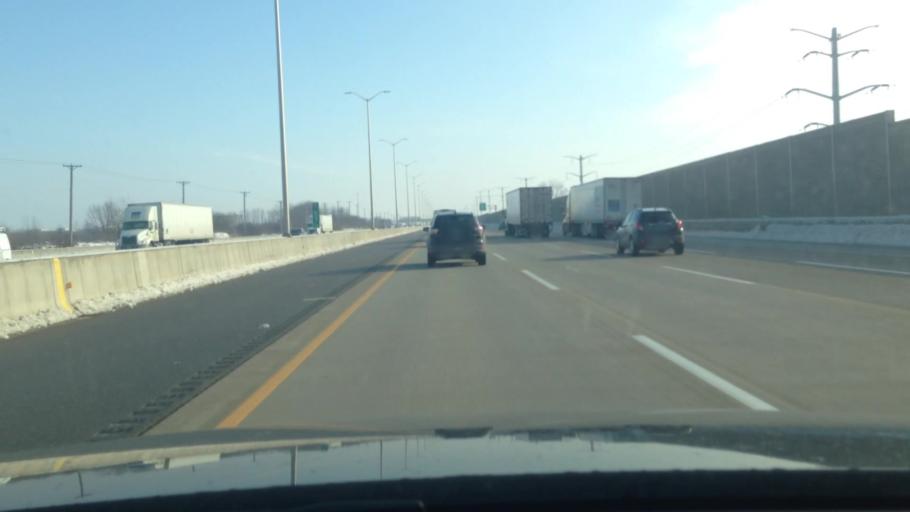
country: US
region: Illinois
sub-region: Kane County
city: East Dundee
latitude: 42.0671
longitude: -88.2373
